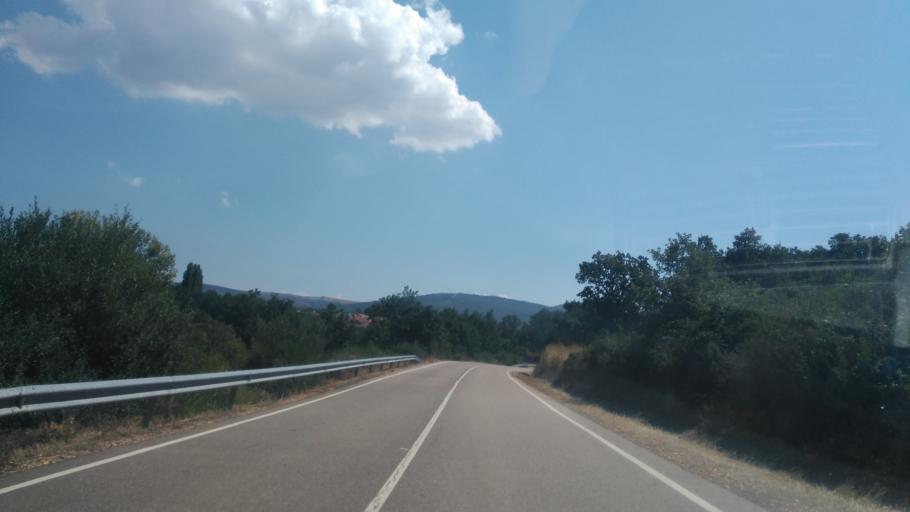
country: ES
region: Castille and Leon
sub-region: Provincia de Salamanca
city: Cereceda de la Sierra
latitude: 40.5665
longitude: -6.1001
